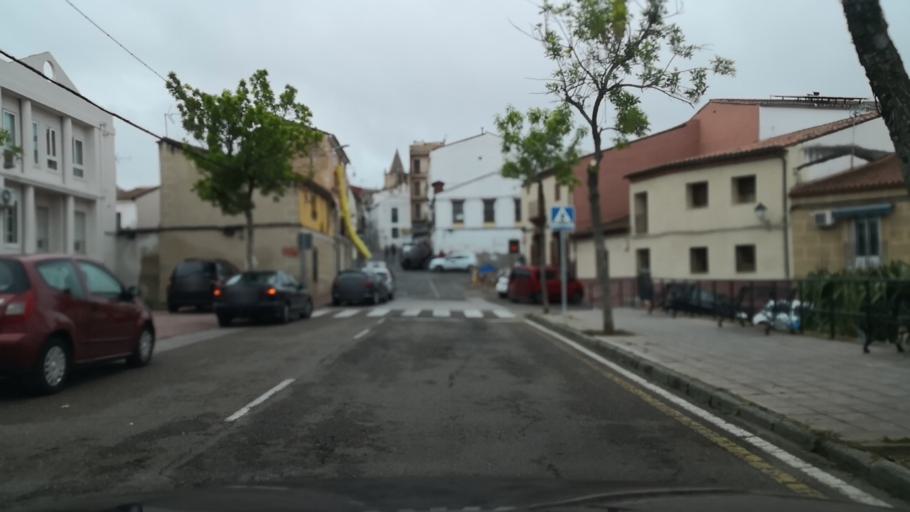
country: ES
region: Extremadura
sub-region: Provincia de Caceres
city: Caceres
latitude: 39.4787
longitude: -6.3694
